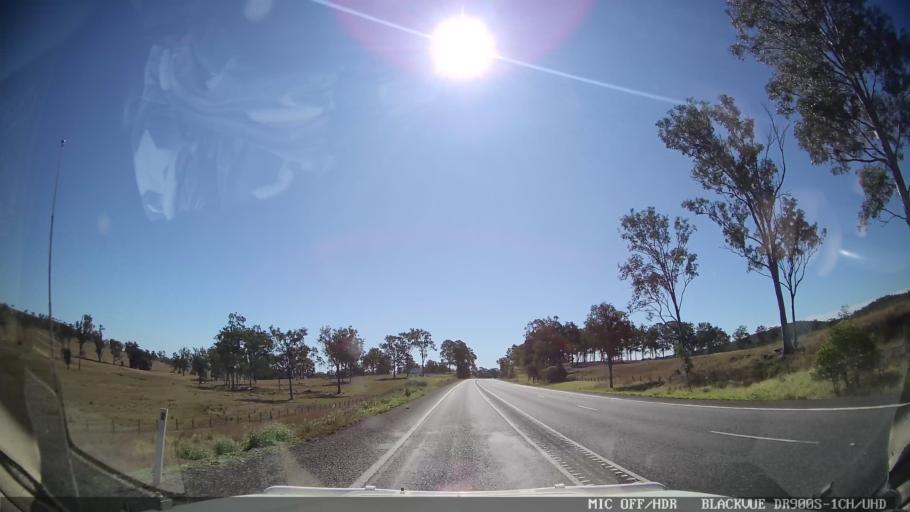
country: AU
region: Queensland
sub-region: Fraser Coast
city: Maryborough
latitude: -25.7750
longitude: 152.5964
